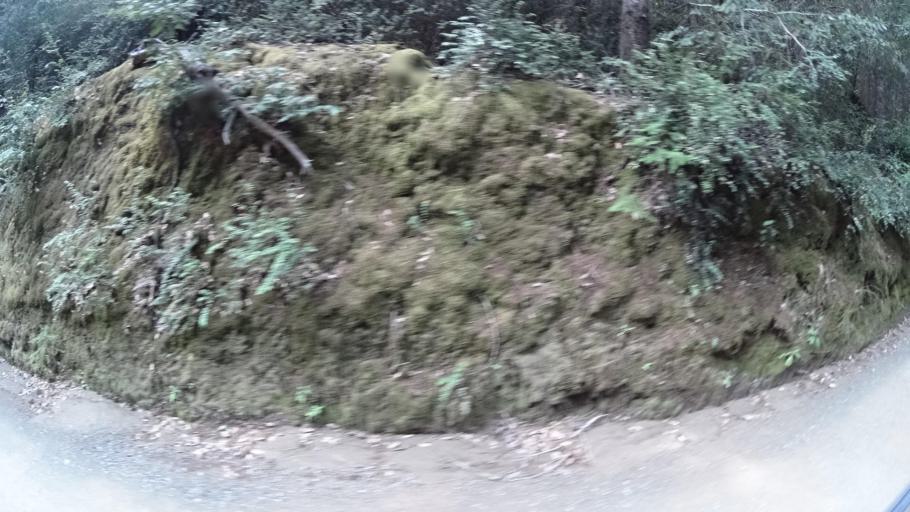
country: US
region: California
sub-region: Humboldt County
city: Redway
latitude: 40.0429
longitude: -123.8443
